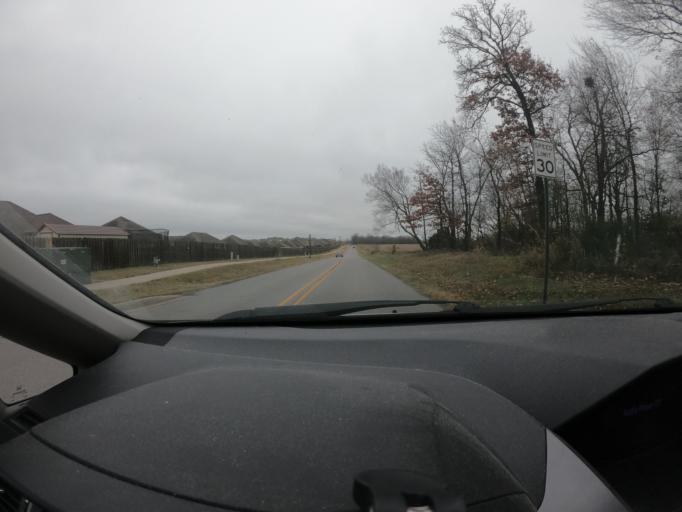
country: US
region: Arkansas
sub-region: Benton County
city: Bentonville
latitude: 36.3503
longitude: -94.2402
